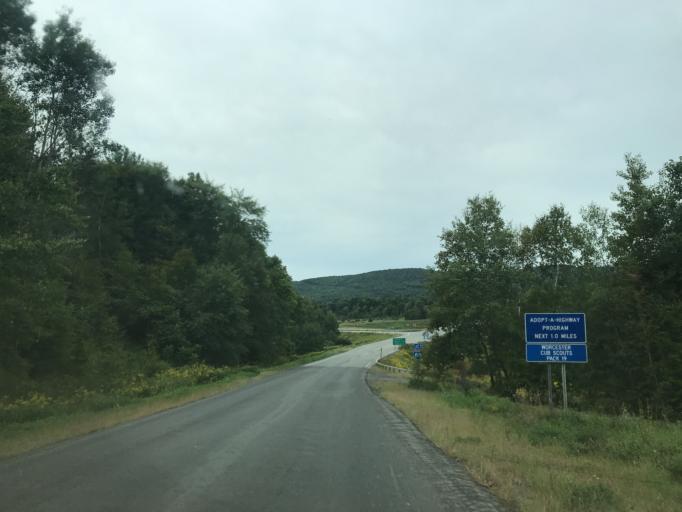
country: US
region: New York
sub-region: Otsego County
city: Worcester
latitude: 42.5910
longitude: -74.7243
